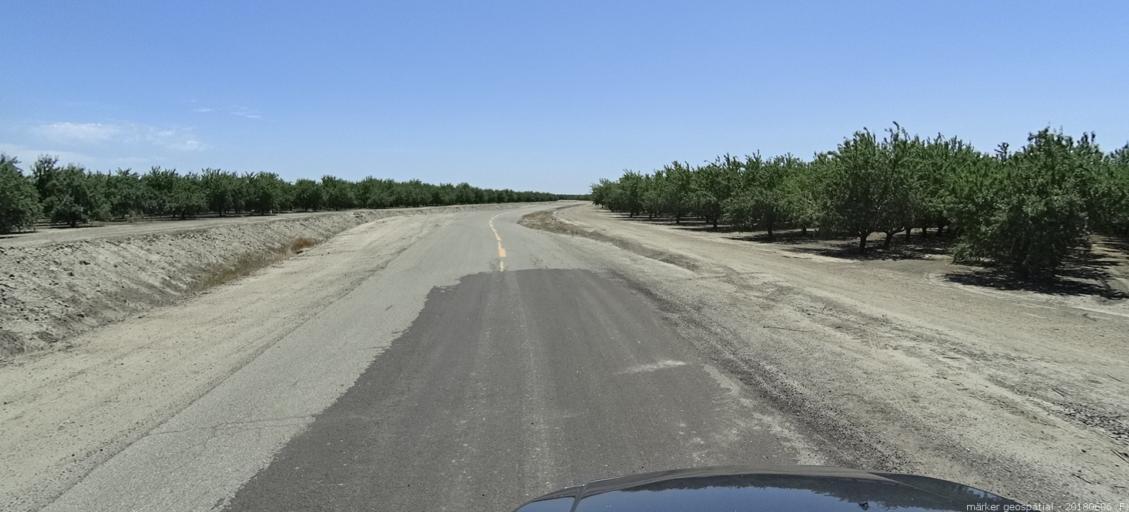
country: US
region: California
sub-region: Fresno County
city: Mendota
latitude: 36.8185
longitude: -120.3690
